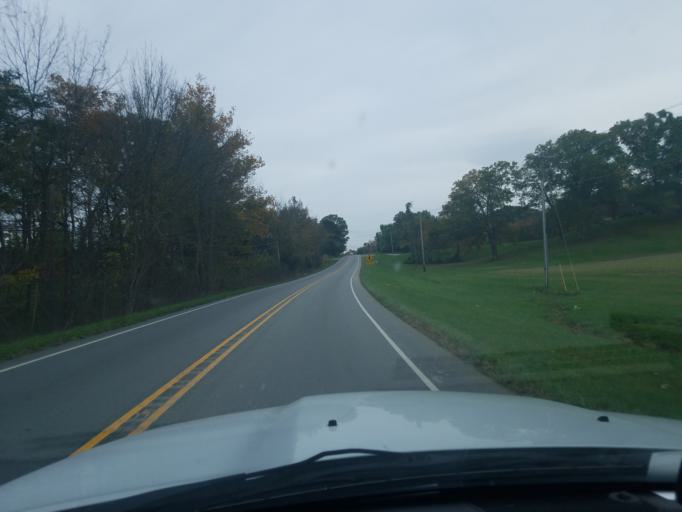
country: US
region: Indiana
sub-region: Clark County
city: Sellersburg
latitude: 38.4424
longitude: -85.8246
